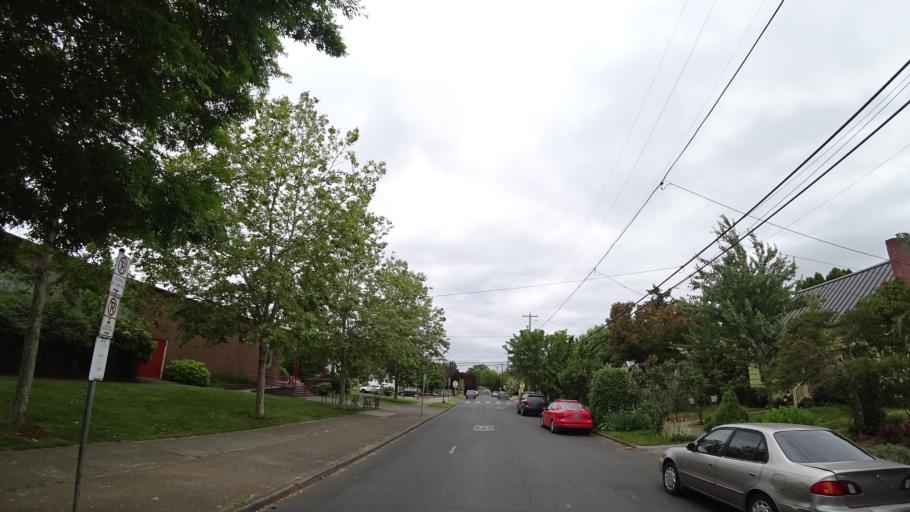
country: US
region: Oregon
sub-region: Multnomah County
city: Portland
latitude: 45.5821
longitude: -122.6999
